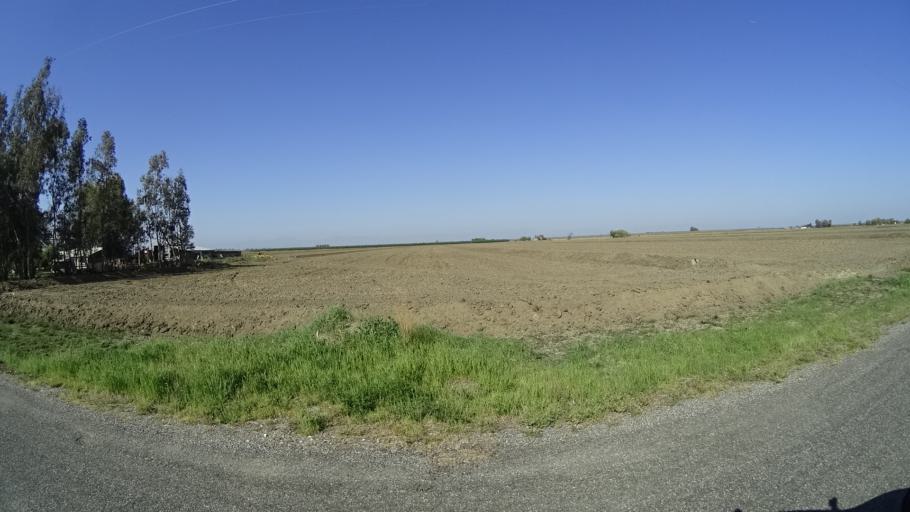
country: US
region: California
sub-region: Glenn County
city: Hamilton City
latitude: 39.6140
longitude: -122.0275
